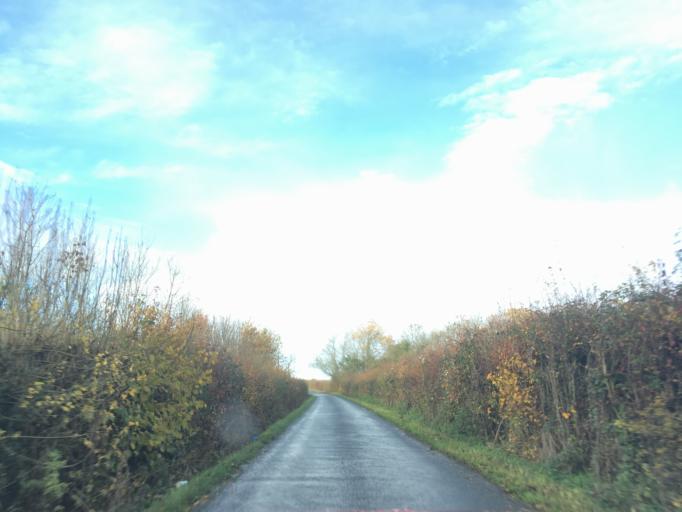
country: GB
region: England
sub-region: South Gloucestershire
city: Hinton
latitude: 51.4812
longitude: -2.4088
